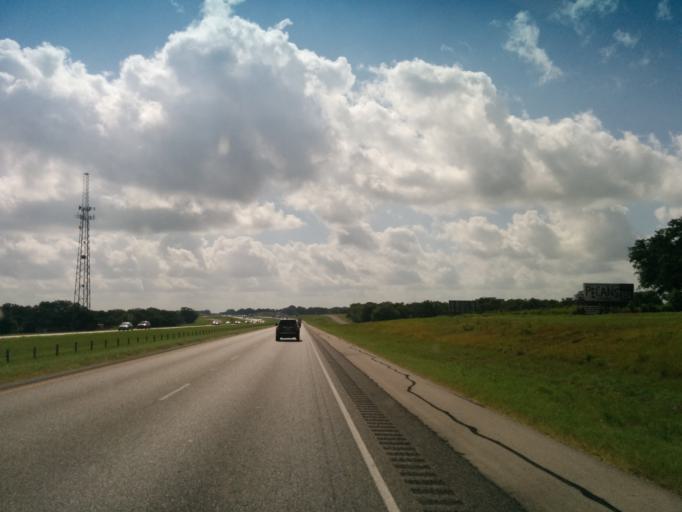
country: US
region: Texas
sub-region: Fayette County
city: Flatonia
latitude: 29.6925
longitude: -97.0143
